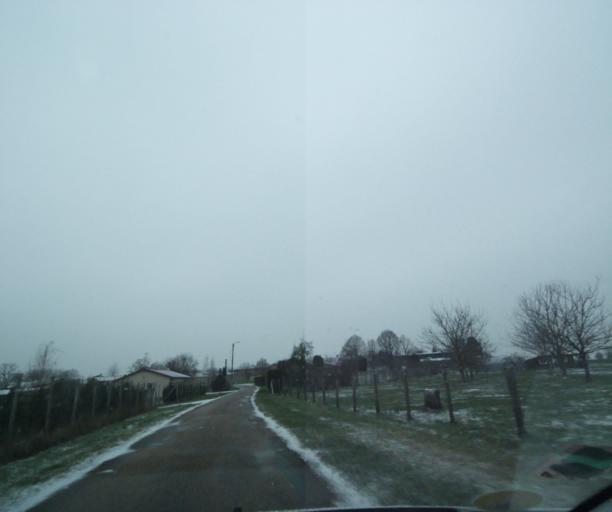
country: FR
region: Champagne-Ardenne
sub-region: Departement de la Haute-Marne
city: Wassy
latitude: 48.4691
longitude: 4.9960
